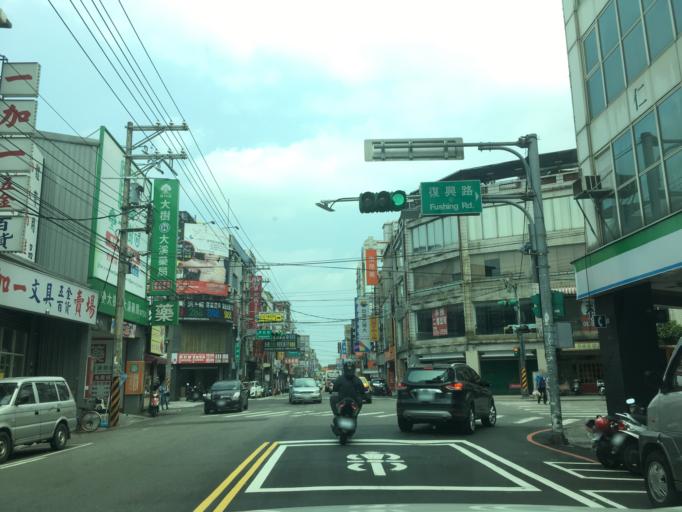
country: TW
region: Taiwan
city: Daxi
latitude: 24.8805
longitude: 121.2887
